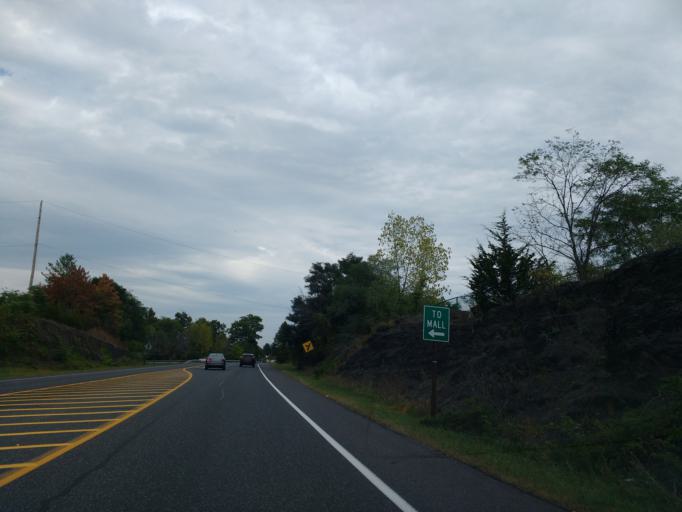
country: US
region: New York
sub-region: Ulster County
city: Lincoln Park
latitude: 41.9617
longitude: -73.9838
